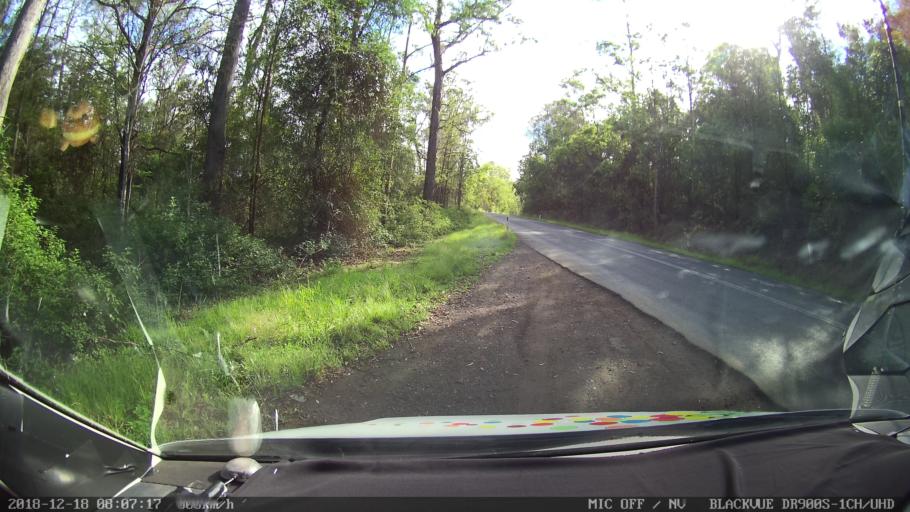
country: AU
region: New South Wales
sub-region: Kyogle
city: Kyogle
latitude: -28.3835
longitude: 152.6455
